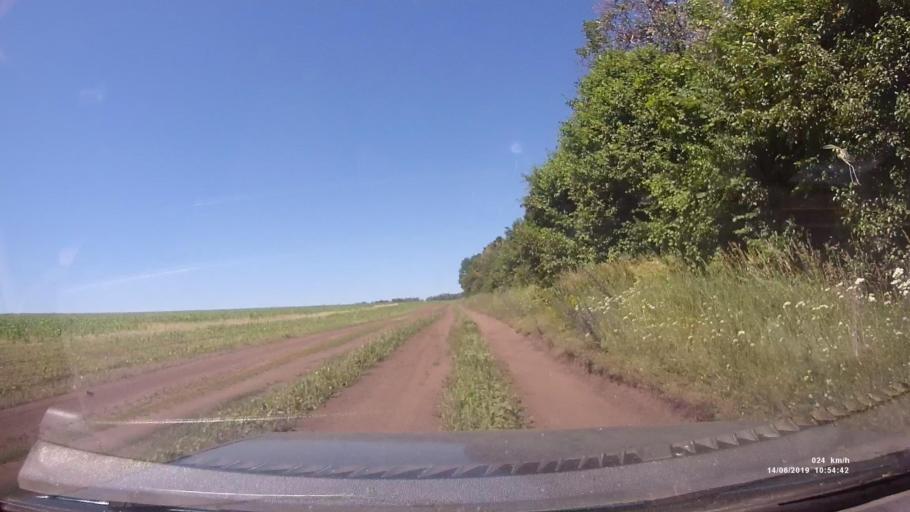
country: RU
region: Rostov
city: Kazanskaya
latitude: 49.8624
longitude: 41.3764
